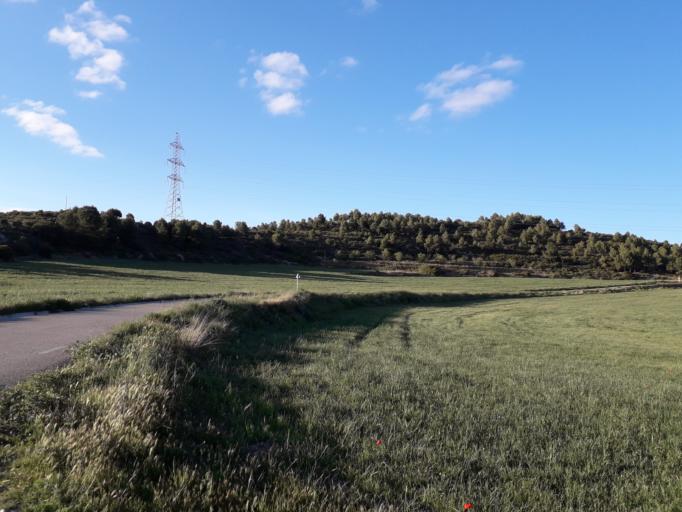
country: ES
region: Catalonia
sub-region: Provincia de Barcelona
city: Jorba
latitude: 41.6214
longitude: 1.5798
